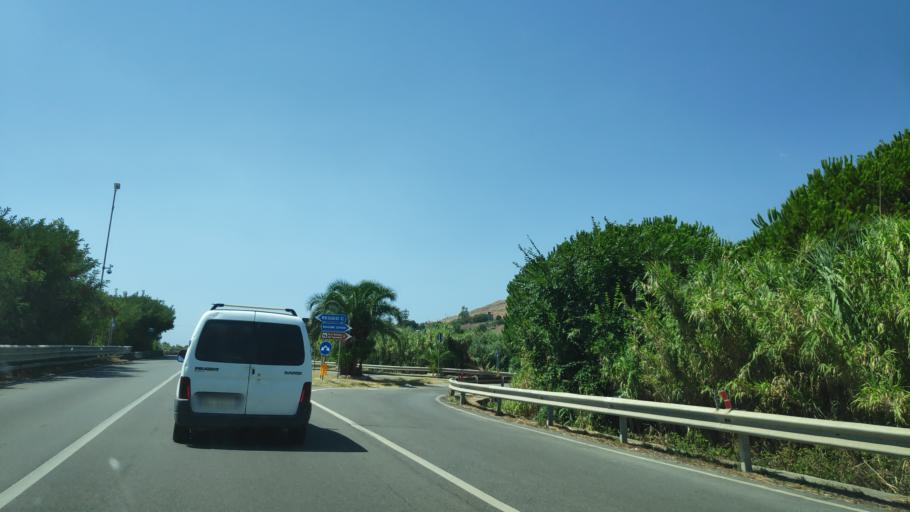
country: IT
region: Calabria
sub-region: Provincia di Reggio Calabria
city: Brancaleone-Marina
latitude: 37.9830
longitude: 16.1157
